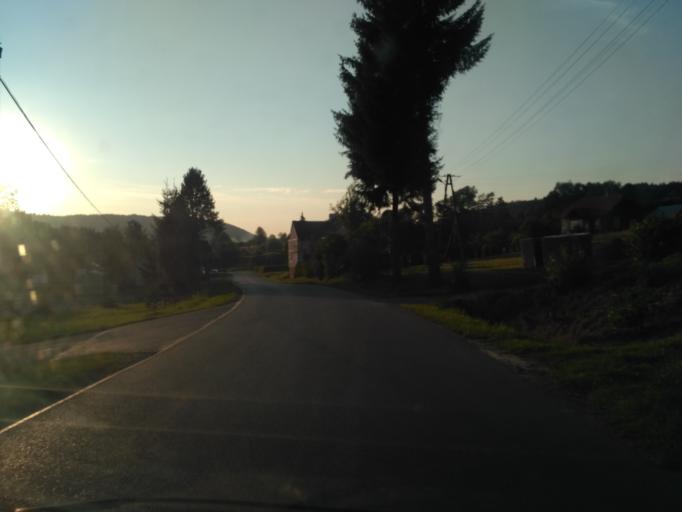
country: PL
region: Subcarpathian Voivodeship
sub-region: Powiat krosnienski
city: Odrzykon
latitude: 49.7756
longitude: 21.7788
